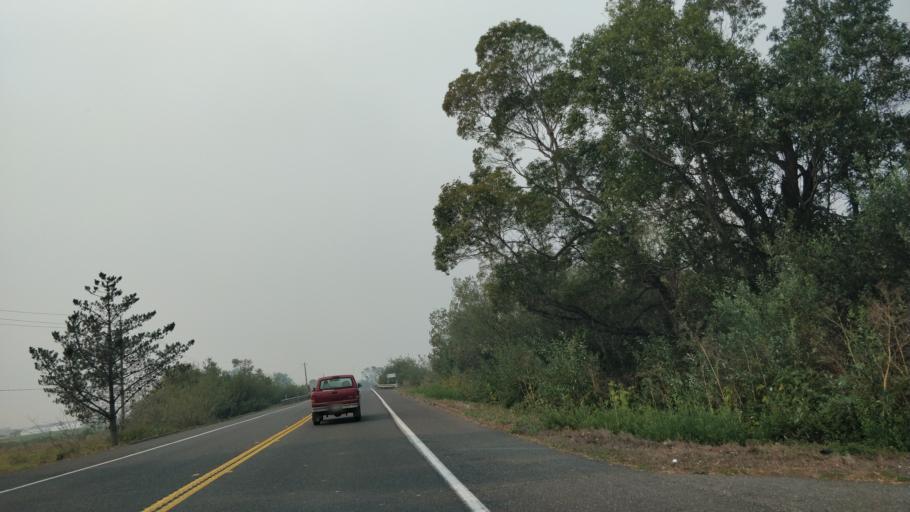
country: US
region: California
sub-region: Humboldt County
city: Ferndale
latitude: 40.5955
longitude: -124.2395
